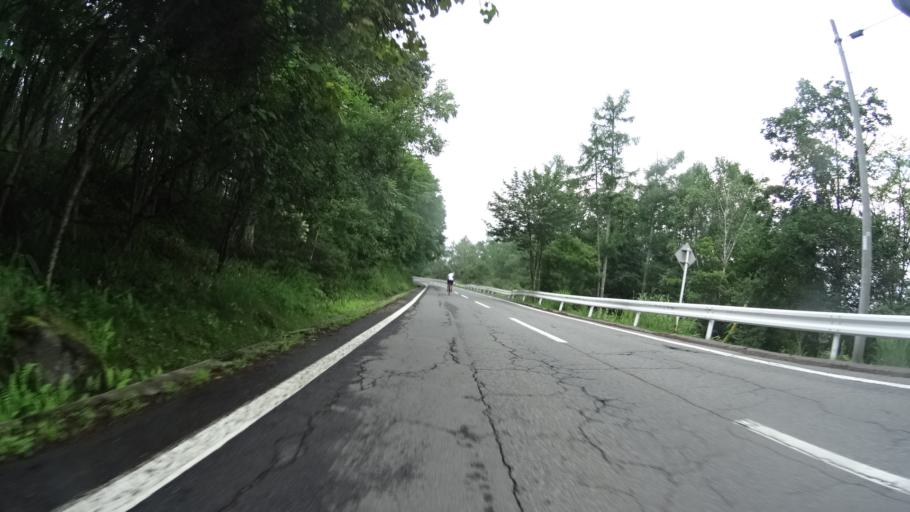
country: JP
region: Nagano
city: Chino
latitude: 36.0422
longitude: 138.2827
